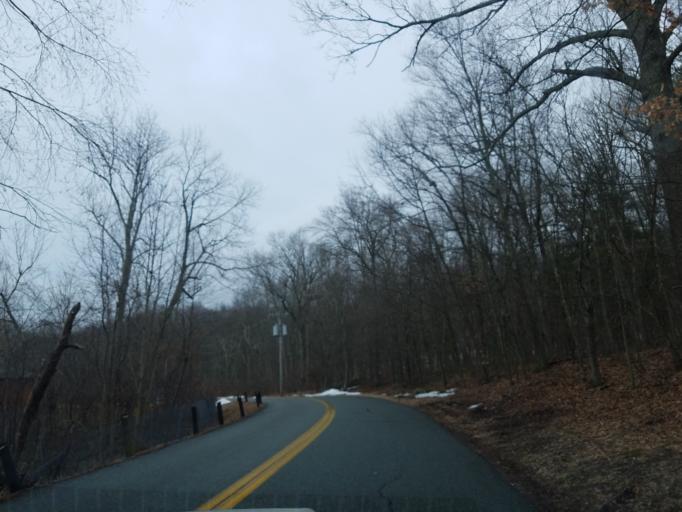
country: US
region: Connecticut
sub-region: Hartford County
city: Glastonbury Center
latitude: 41.6707
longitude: -72.5516
